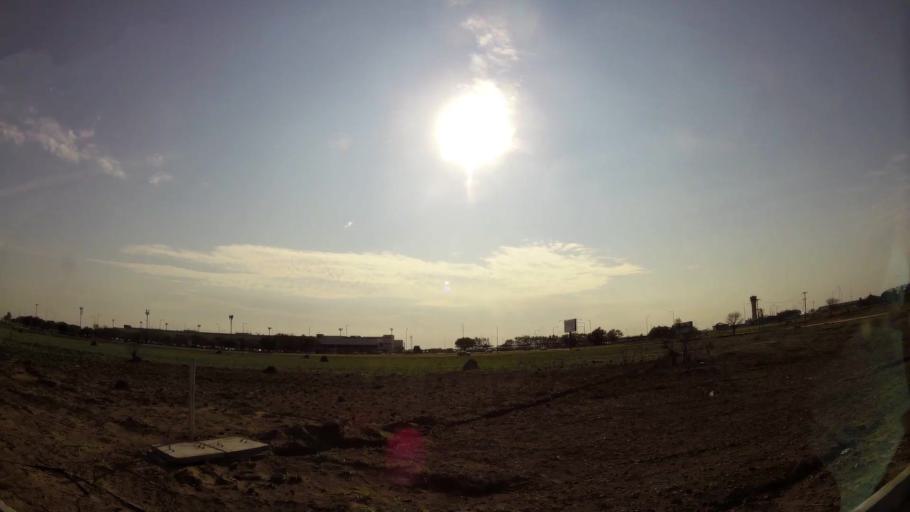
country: BO
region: Santa Cruz
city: La Belgica
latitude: -17.6511
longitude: -63.1419
